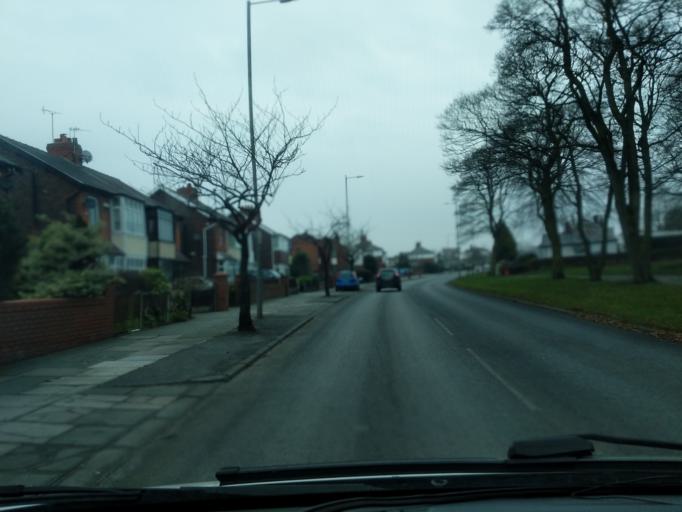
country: GB
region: England
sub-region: St. Helens
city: St Helens
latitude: 53.4687
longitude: -2.7289
